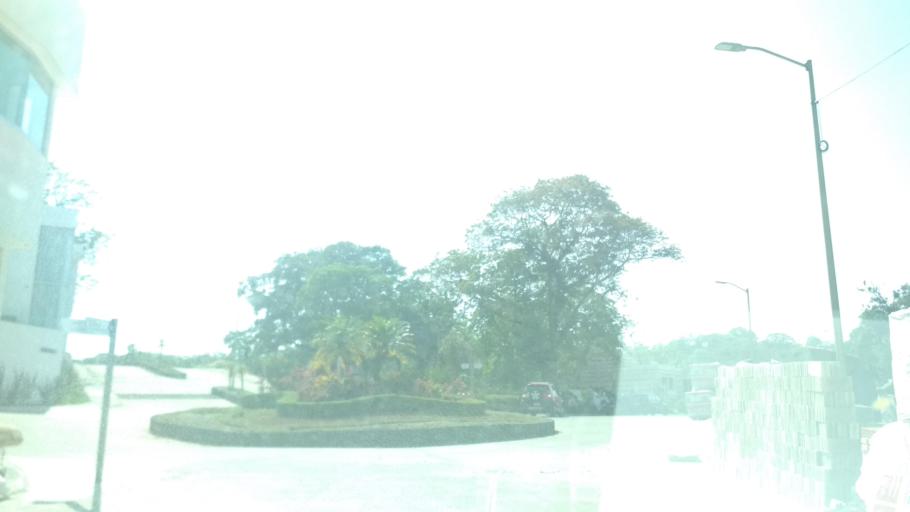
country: MX
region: Veracruz
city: El Castillo
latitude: 19.5287
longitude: -96.8654
